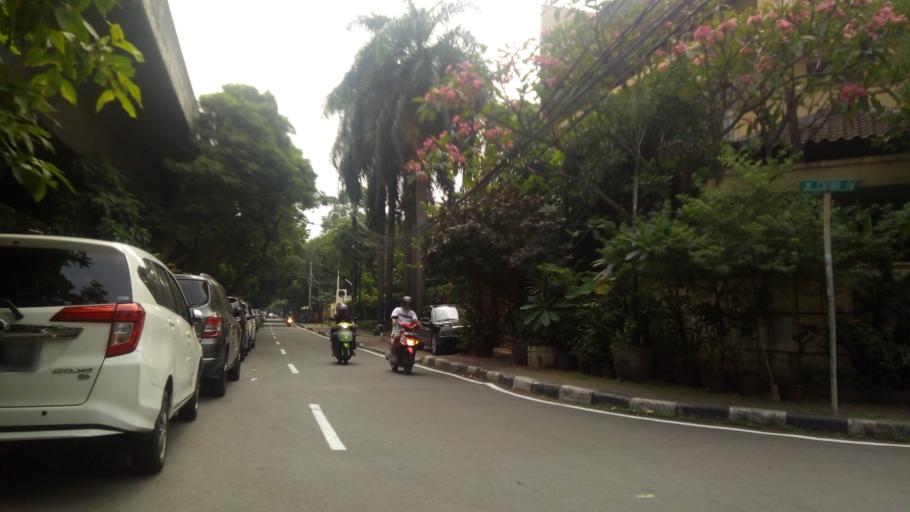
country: ID
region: Jakarta Raya
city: Jakarta
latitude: -6.1941
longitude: 106.8381
